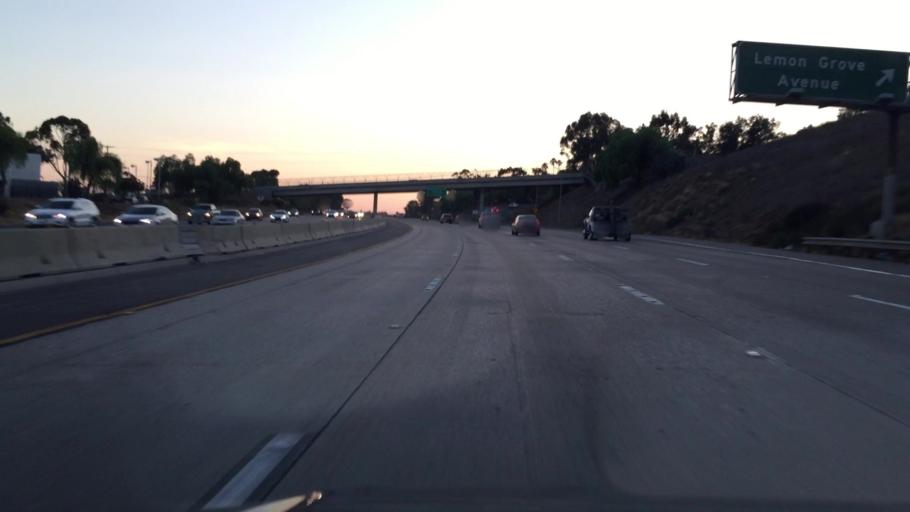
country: US
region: California
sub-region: San Diego County
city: Lemon Grove
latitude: 32.7471
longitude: -117.0286
